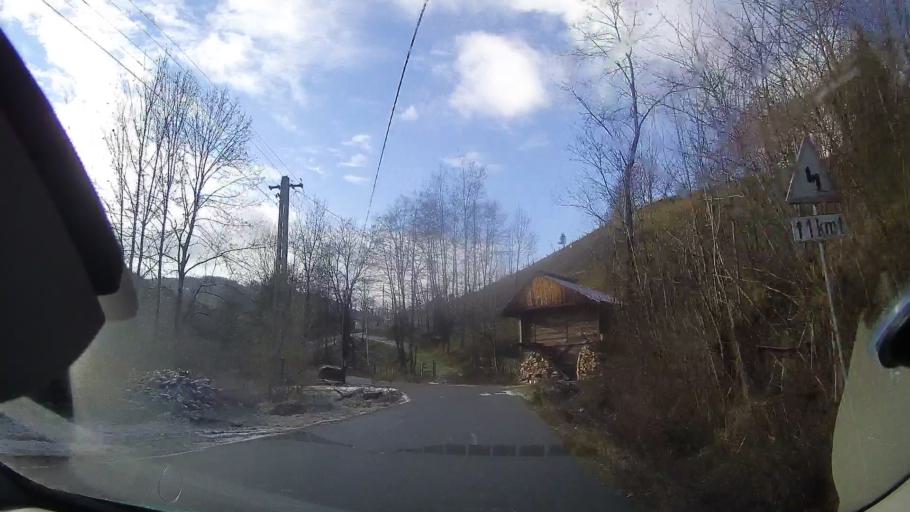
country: RO
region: Alba
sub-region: Comuna Sohodol
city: Sohodol
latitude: 46.3428
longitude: 23.0153
